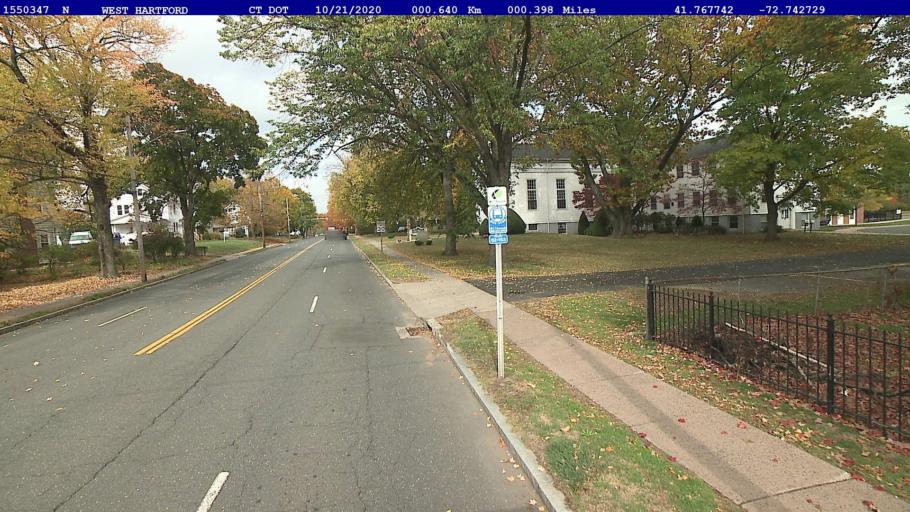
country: US
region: Connecticut
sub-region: Hartford County
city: West Hartford
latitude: 41.7677
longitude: -72.7427
